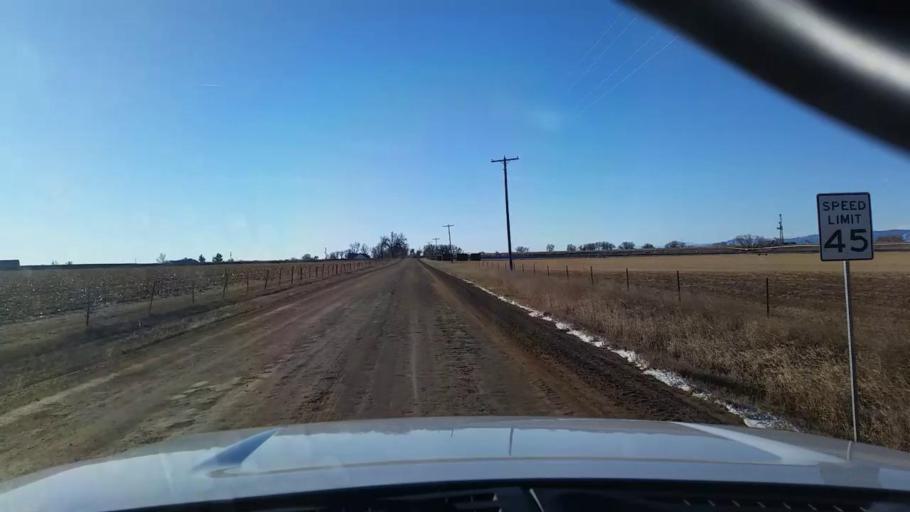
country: US
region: Colorado
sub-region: Larimer County
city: Wellington
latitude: 40.7692
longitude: -105.0382
